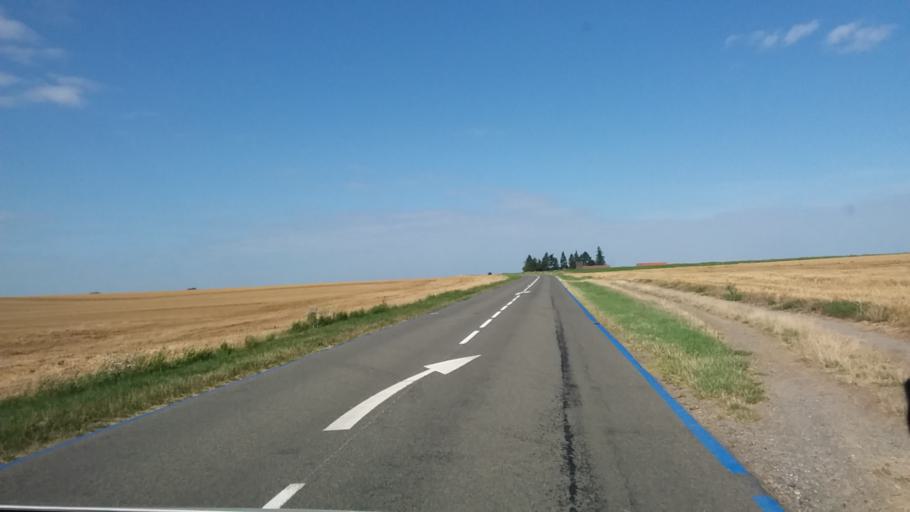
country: FR
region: Picardie
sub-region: Departement de l'Aisne
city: Bruyeres-et-Montberault
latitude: 49.4413
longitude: 3.7205
